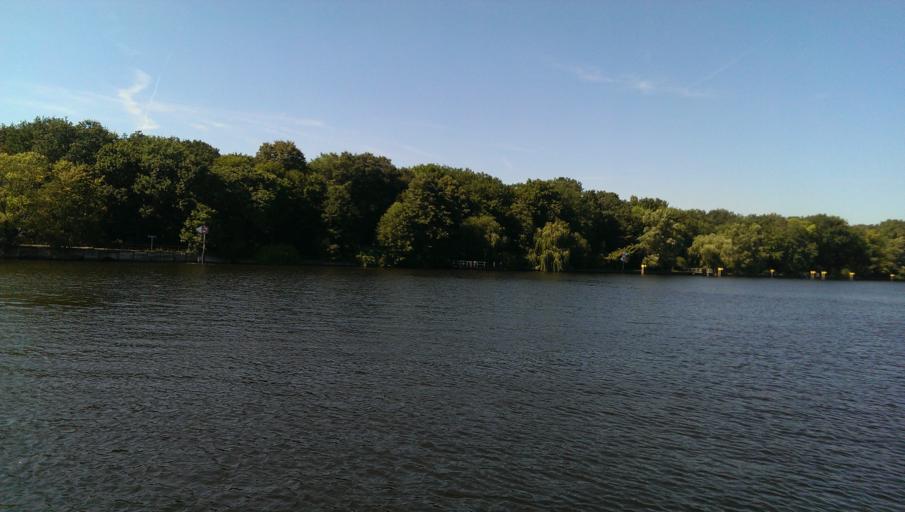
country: DE
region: Berlin
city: Baumschulenweg
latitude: 52.4722
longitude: 13.4967
